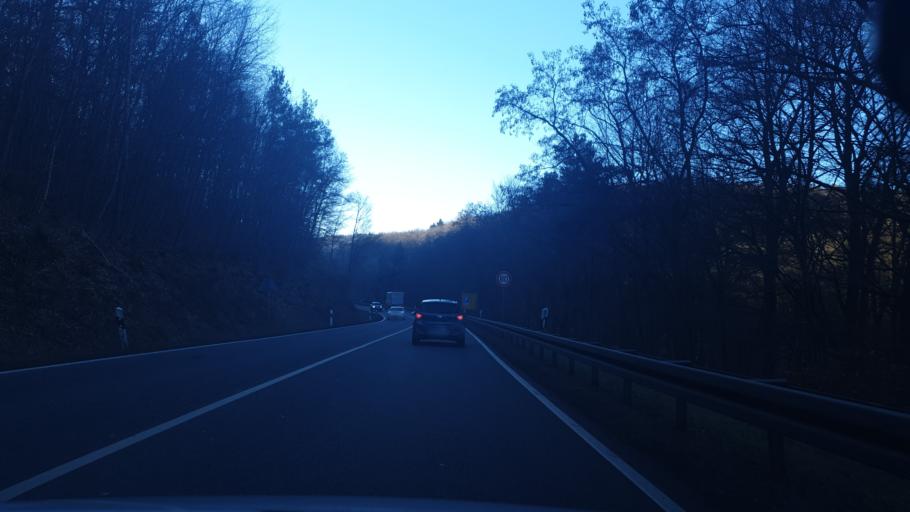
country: DE
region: Hesse
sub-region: Regierungsbezirk Darmstadt
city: Idstein
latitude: 50.2003
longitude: 8.2447
